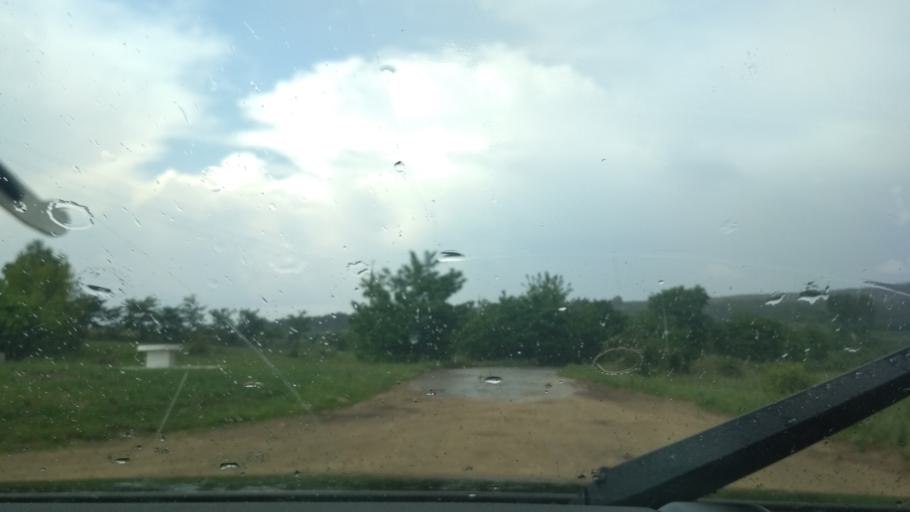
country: MD
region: Singerei
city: Biruinta
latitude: 47.7414
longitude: 28.1365
